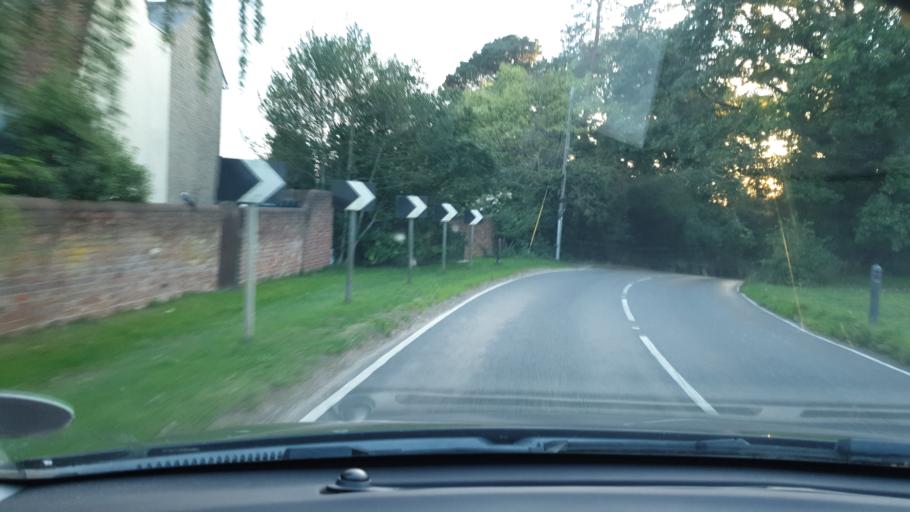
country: GB
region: England
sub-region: Essex
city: Rowhedge
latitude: 51.8975
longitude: 0.9535
